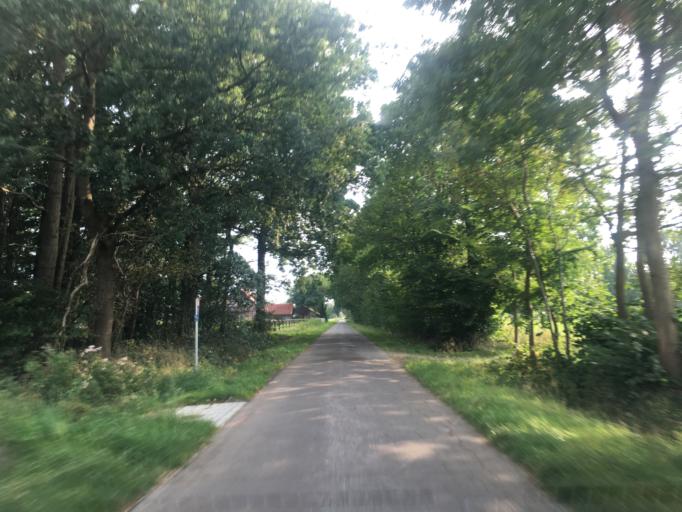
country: DE
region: North Rhine-Westphalia
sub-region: Regierungsbezirk Munster
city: Greven
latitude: 52.0451
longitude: 7.5833
